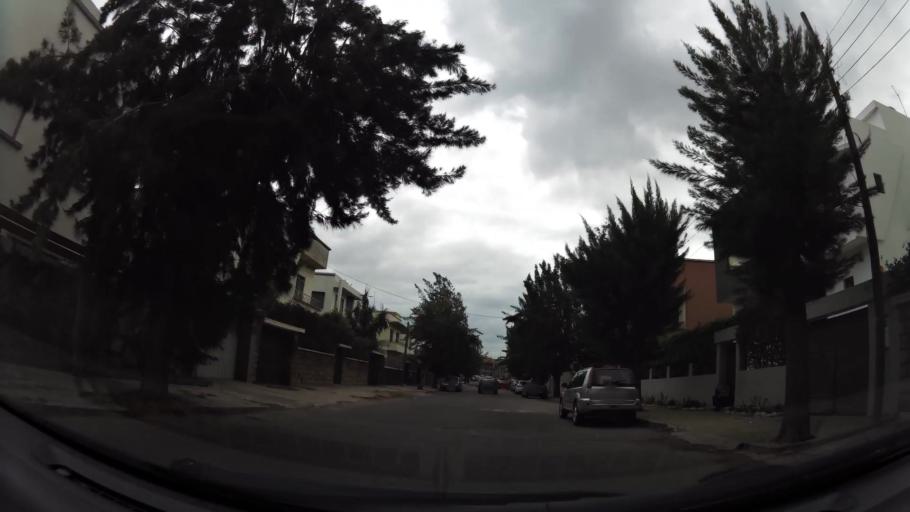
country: MA
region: Grand Casablanca
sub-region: Casablanca
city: Casablanca
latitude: 33.5580
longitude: -7.6127
